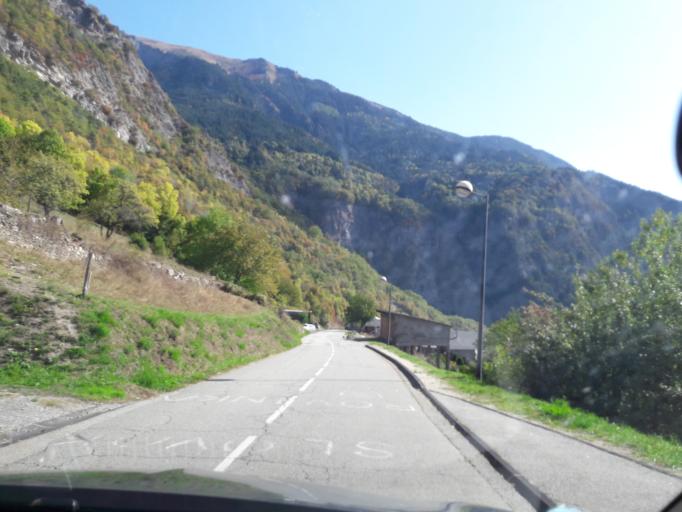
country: FR
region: Rhone-Alpes
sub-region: Departement de la Savoie
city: Saint-Jean-de-Maurienne
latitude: 45.3061
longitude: 6.3613
